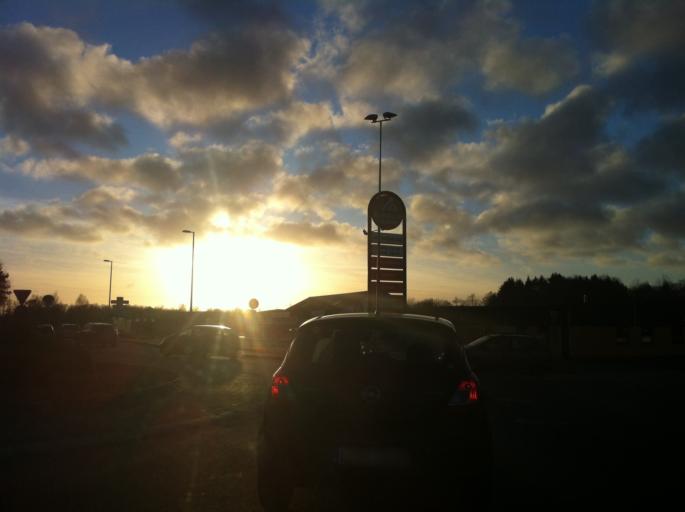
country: SE
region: Skane
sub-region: Hoors Kommun
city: Hoeoer
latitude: 55.9653
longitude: 13.5773
